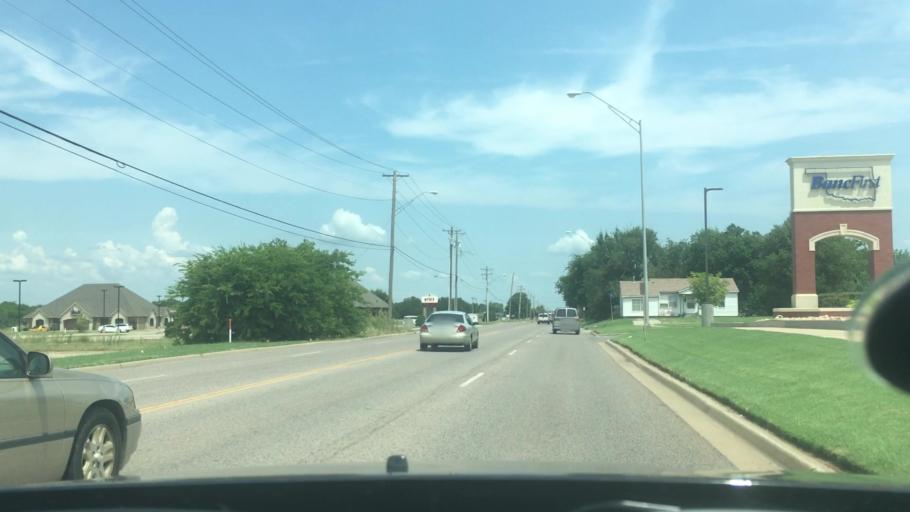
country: US
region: Oklahoma
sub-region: Pottawatomie County
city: Shawnee
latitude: 35.3649
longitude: -96.9298
